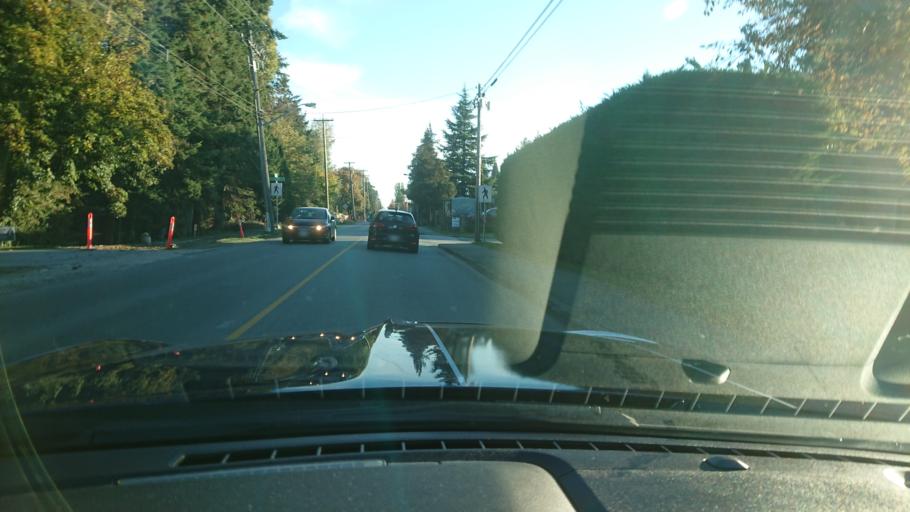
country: CA
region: British Columbia
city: Richmond
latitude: 49.1281
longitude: -123.1590
